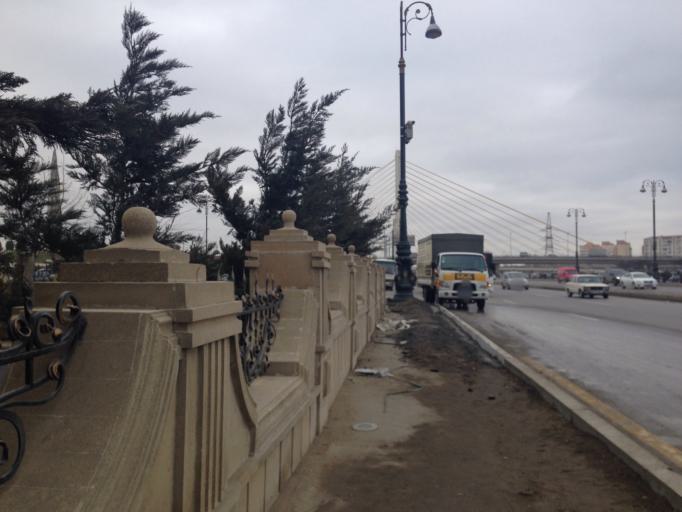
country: AZ
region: Baki
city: Sabuncu
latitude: 40.4209
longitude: 49.9160
